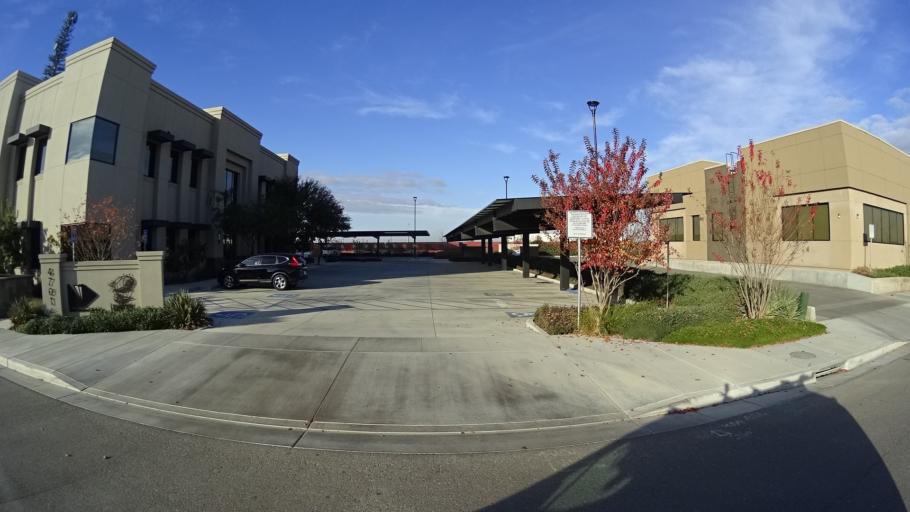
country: US
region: California
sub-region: Kern County
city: Rosedale
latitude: 35.3119
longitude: -119.1321
